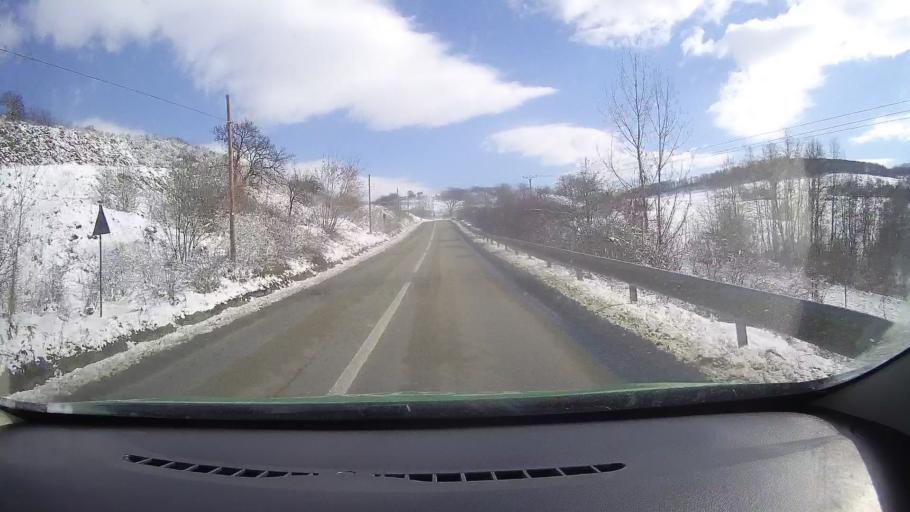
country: RO
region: Sibiu
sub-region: Comuna Barghis
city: Barghis
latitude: 45.9828
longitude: 24.5089
